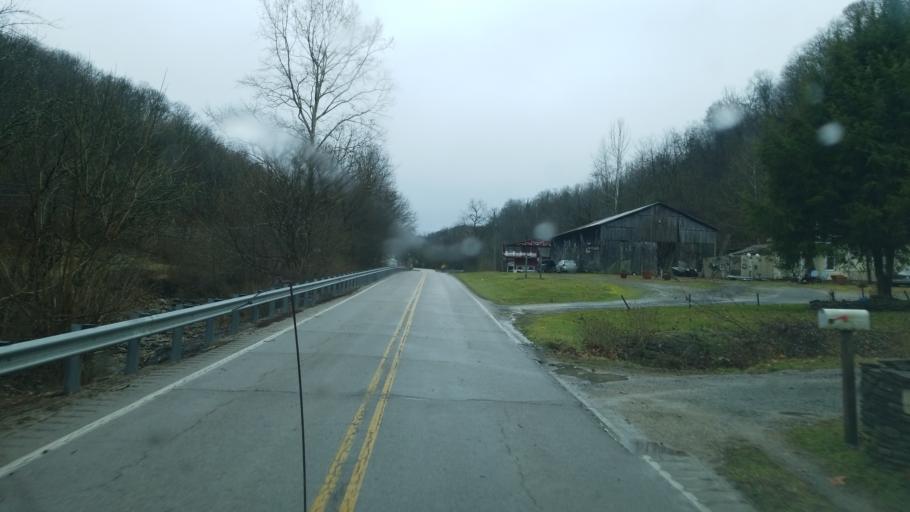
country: US
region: Kentucky
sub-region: Mason County
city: Maysville
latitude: 38.6249
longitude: -83.7050
